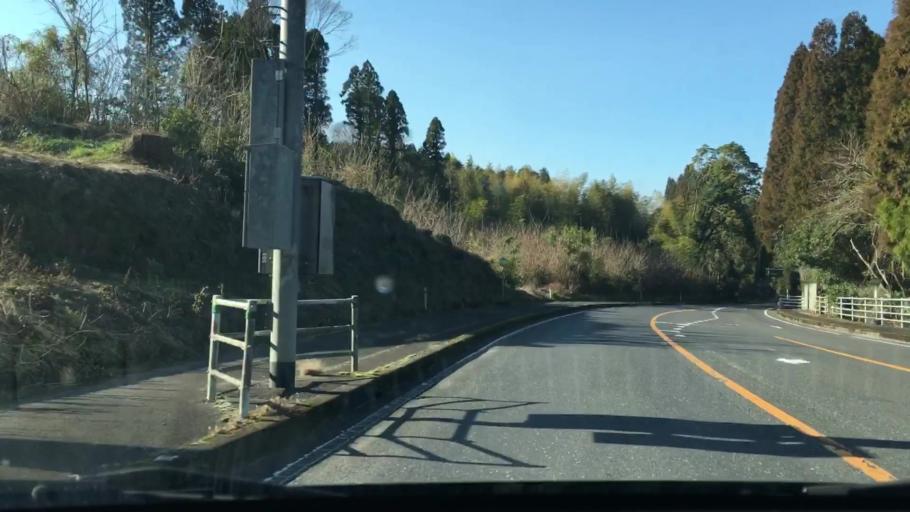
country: JP
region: Kagoshima
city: Sueyoshicho-ninokata
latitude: 31.6745
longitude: 130.9266
